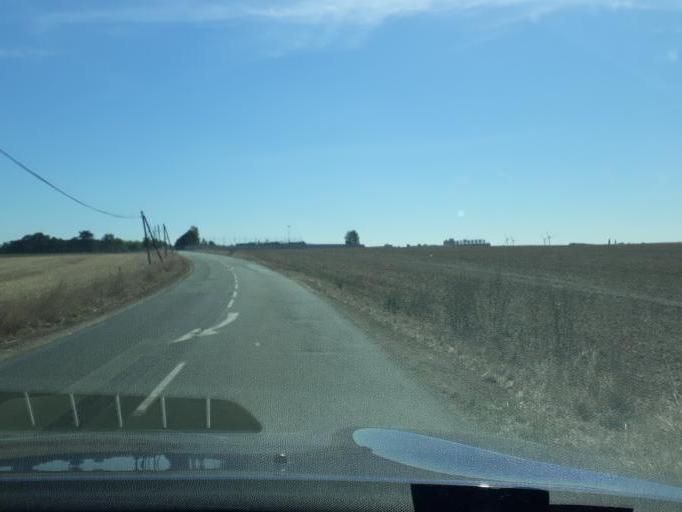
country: FR
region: Centre
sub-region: Departement du Loir-et-Cher
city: Ouzouer-le-Marche
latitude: 47.9252
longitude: 1.5202
